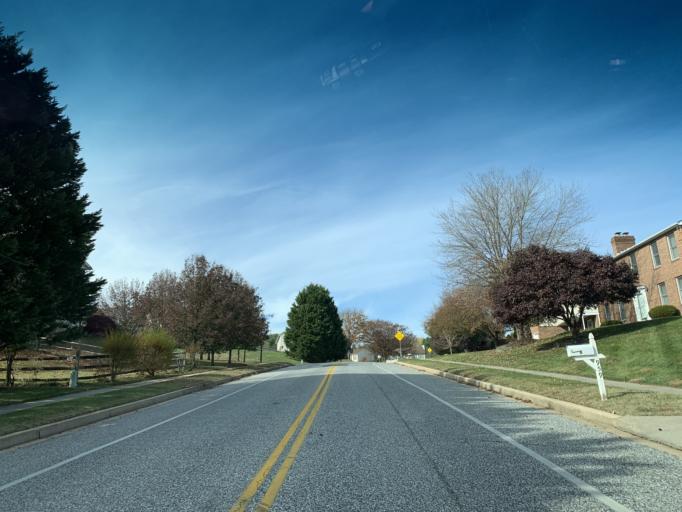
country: US
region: Maryland
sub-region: Harford County
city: South Bel Air
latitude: 39.5305
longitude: -76.3221
